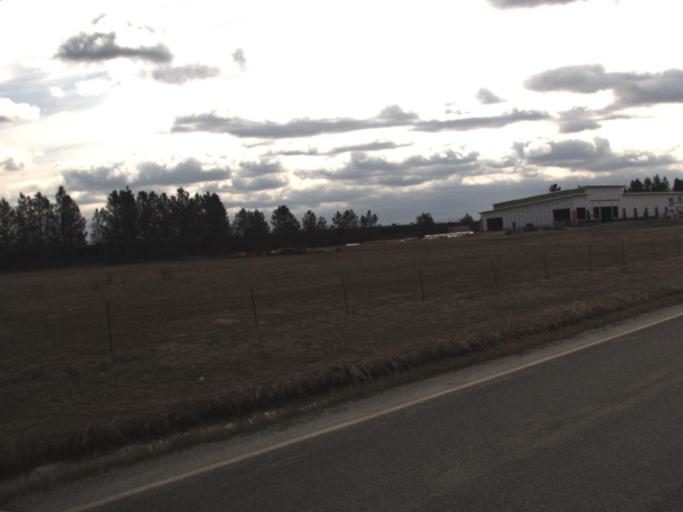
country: US
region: Washington
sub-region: Pend Oreille County
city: Newport
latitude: 48.3519
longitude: -117.3046
